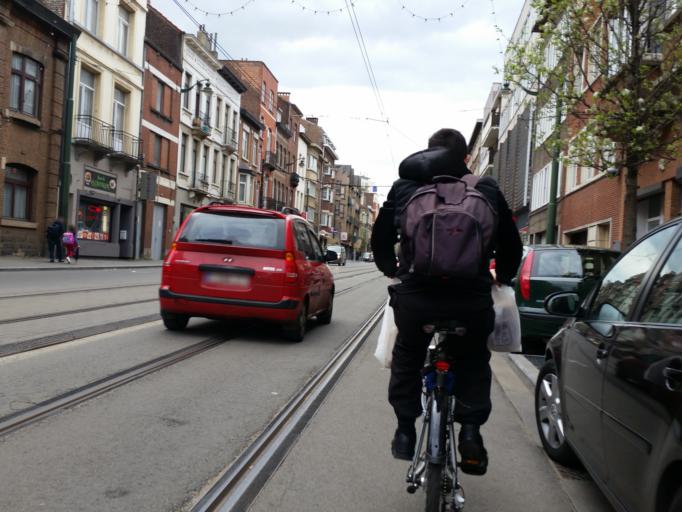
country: BE
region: Brussels Capital
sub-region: Bruxelles-Capitale
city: Brussels
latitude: 50.8580
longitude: 4.3178
